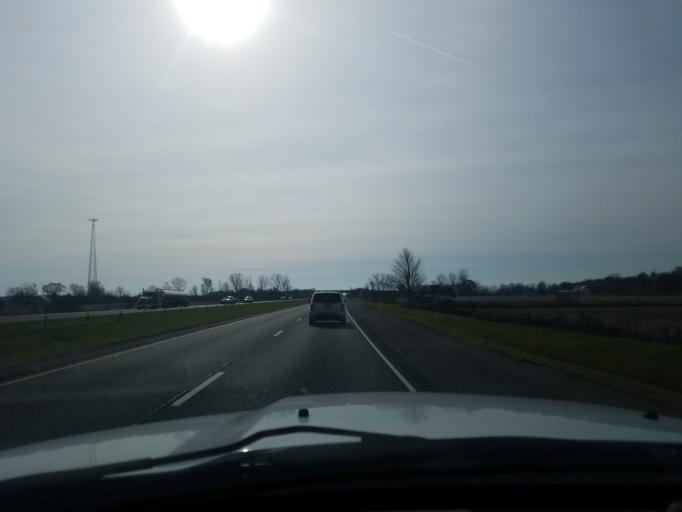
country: US
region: Indiana
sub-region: Delaware County
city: Daleville
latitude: 40.1830
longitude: -85.5625
